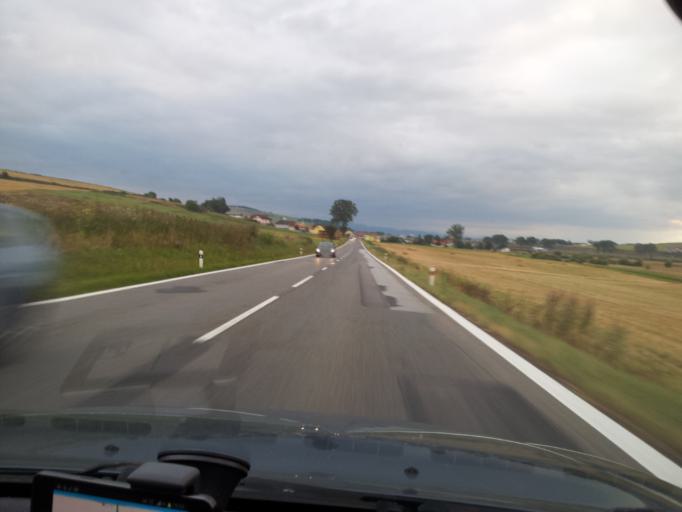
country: SK
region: Presovsky
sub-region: Okres Presov
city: Kezmarok
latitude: 49.1218
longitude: 20.3897
